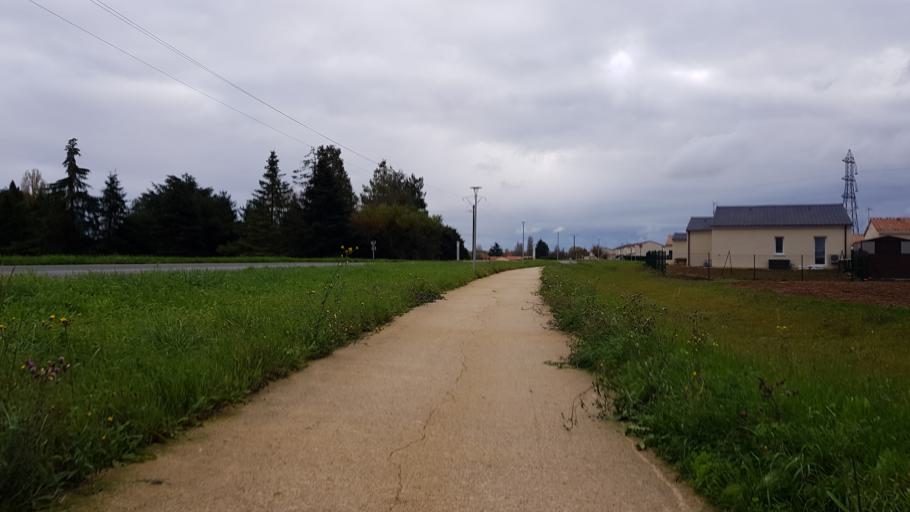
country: FR
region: Poitou-Charentes
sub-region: Departement de la Vienne
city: Chasseneuil-du-Poitou
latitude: 46.6625
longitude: 0.3807
